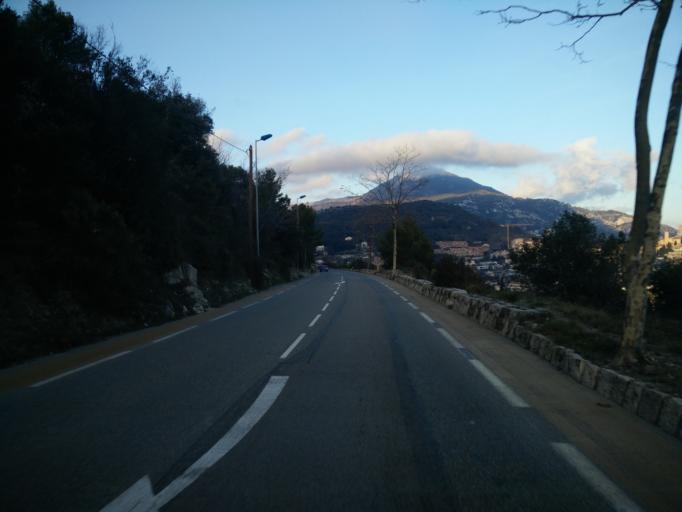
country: FR
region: Provence-Alpes-Cote d'Azur
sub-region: Departement des Alpes-Maritimes
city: La Turbie
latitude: 43.7392
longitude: 7.3897
